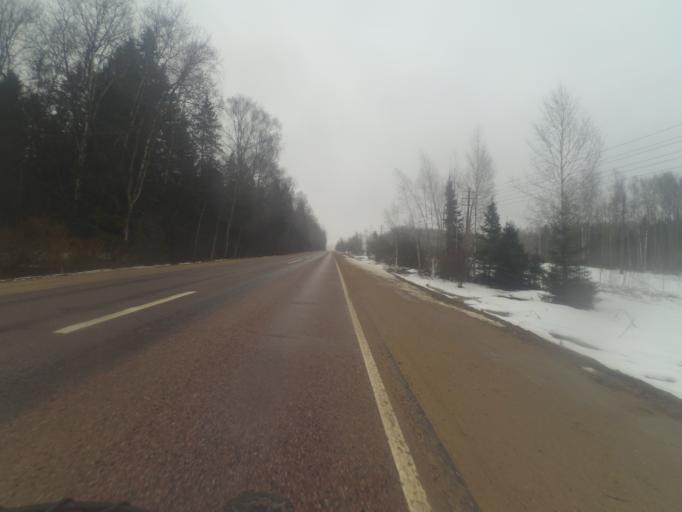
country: RU
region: Moskovskaya
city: Avtopoligon
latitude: 56.2657
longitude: 37.3211
